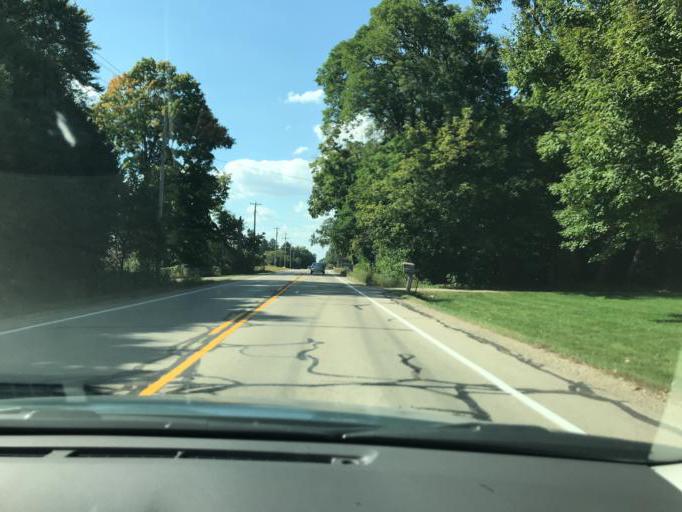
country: US
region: Wisconsin
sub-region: Walworth County
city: Williams Bay
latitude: 42.6081
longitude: -88.5585
